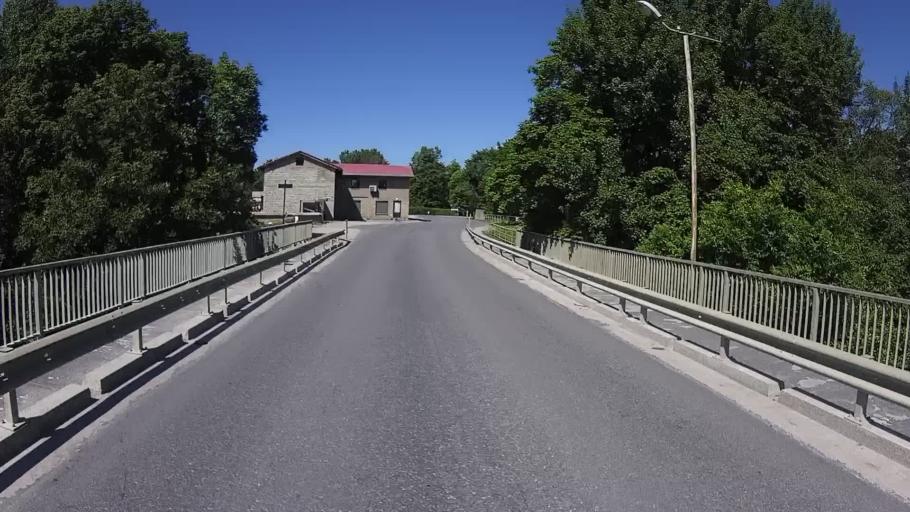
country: EE
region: Laeaene-Virumaa
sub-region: Viru-Nigula vald
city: Kunda
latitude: 59.4991
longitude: 26.5394
